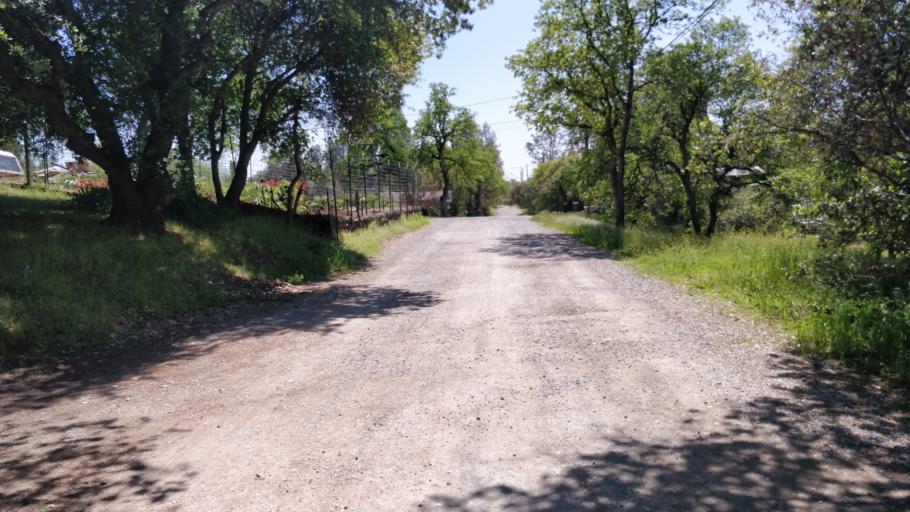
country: US
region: California
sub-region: Shasta County
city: Shasta Lake
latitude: 40.6685
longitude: -122.3560
